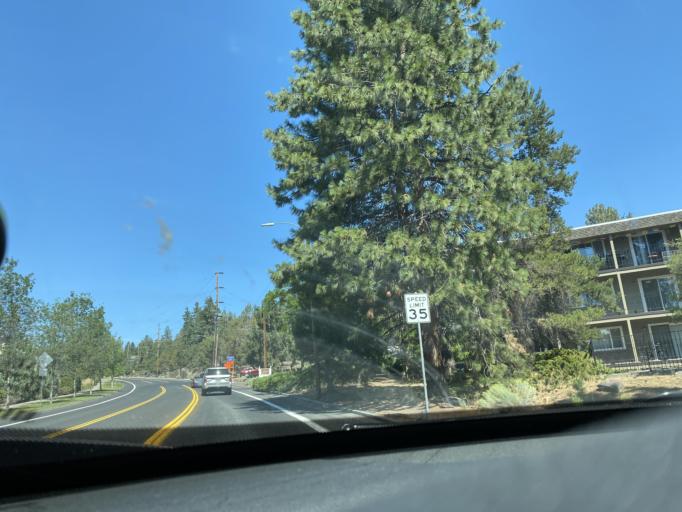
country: US
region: Oregon
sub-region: Deschutes County
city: Bend
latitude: 44.0634
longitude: -121.3385
